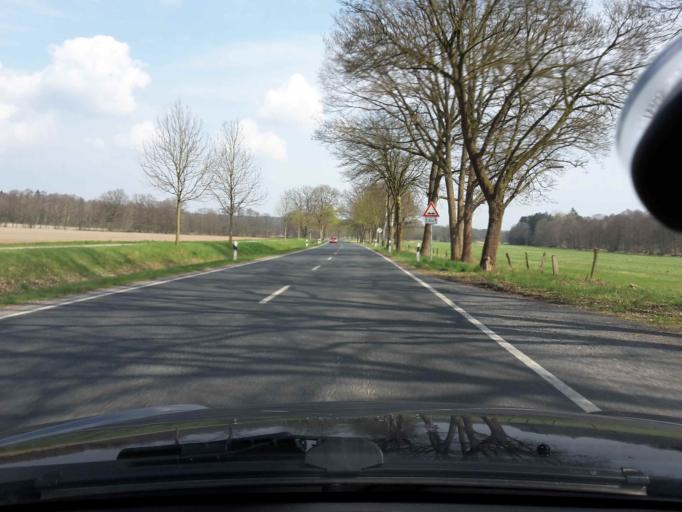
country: DE
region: Lower Saxony
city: Jesteburg
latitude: 53.2946
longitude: 9.9258
